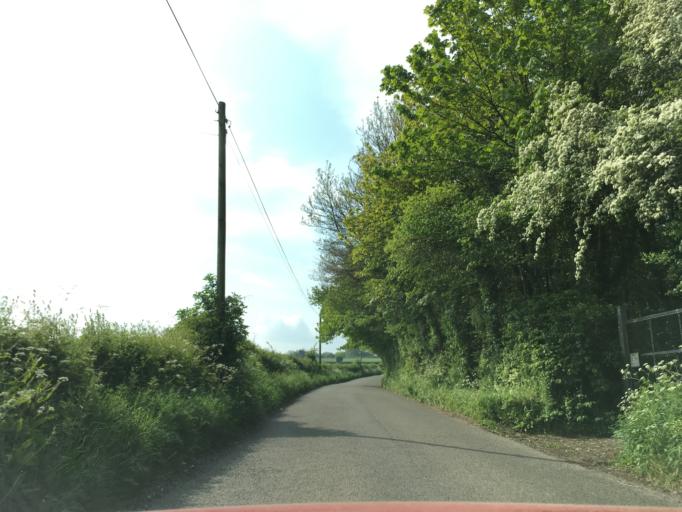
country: GB
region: England
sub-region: North Somerset
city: Butcombe
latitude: 51.4001
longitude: -2.7143
